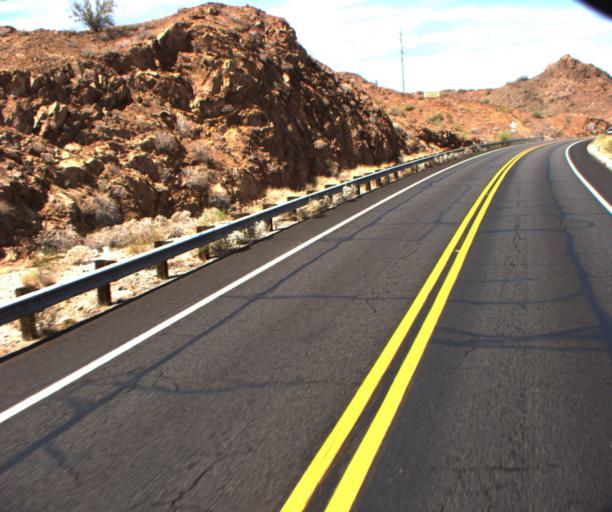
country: US
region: Arizona
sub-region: La Paz County
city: Cienega Springs
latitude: 34.2907
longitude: -114.1308
